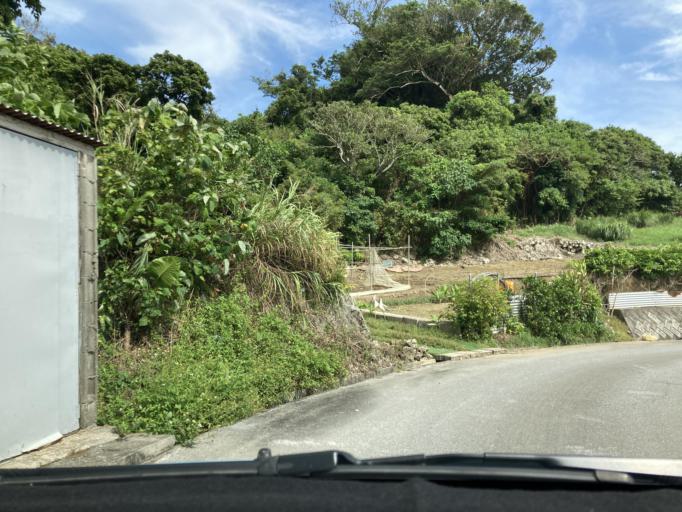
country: JP
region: Okinawa
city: Ginowan
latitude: 26.1597
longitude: 127.8121
